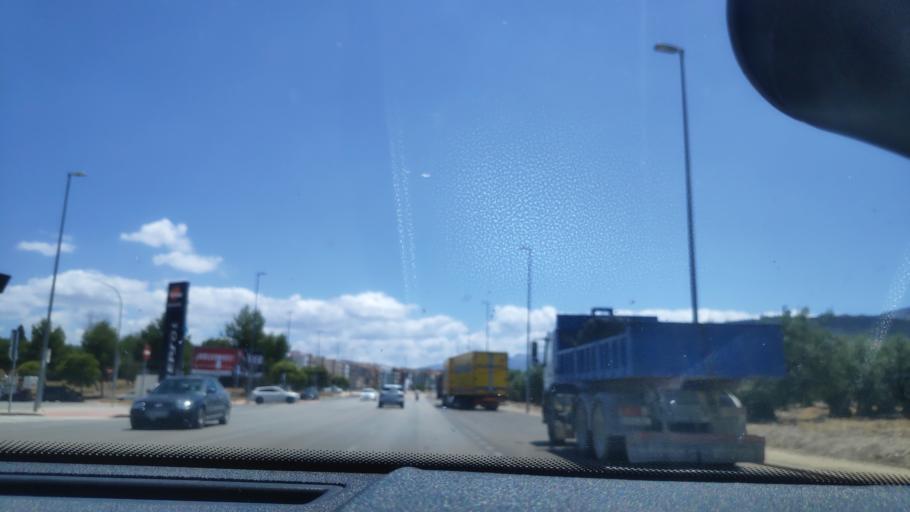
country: ES
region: Andalusia
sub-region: Provincia de Jaen
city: Jaen
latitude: 37.7934
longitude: -3.7922
